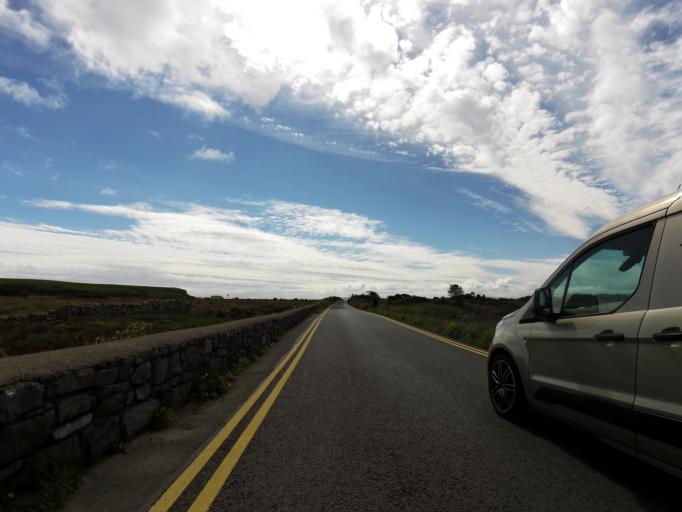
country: IE
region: Connaught
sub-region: County Galway
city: Bearna
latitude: 53.2536
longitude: -9.1298
